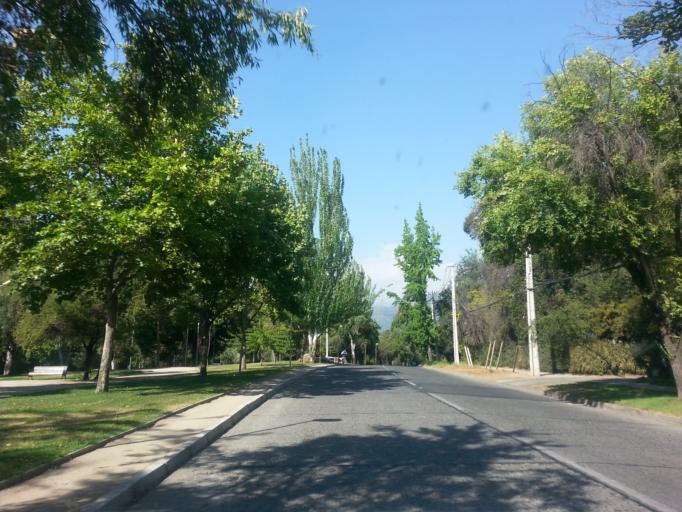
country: CL
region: Santiago Metropolitan
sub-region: Provincia de Santiago
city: Villa Presidente Frei, Nunoa, Santiago, Chile
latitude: -33.3872
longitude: -70.5233
